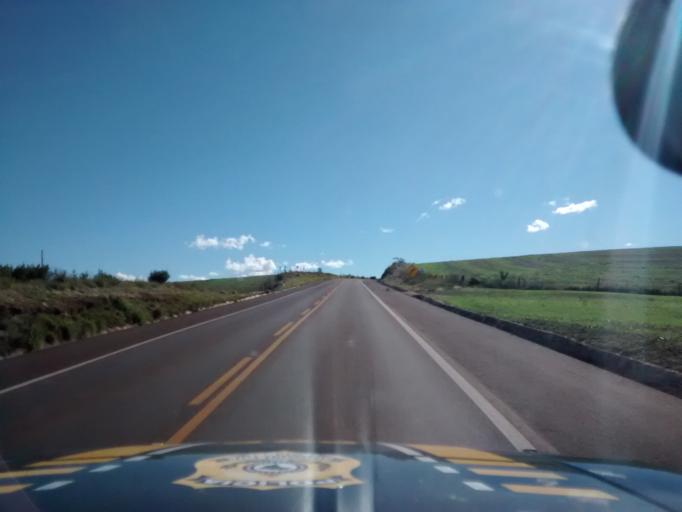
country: BR
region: Rio Grande do Sul
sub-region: Lagoa Vermelha
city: Lagoa Vermelha
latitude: -28.3168
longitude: -51.3555
